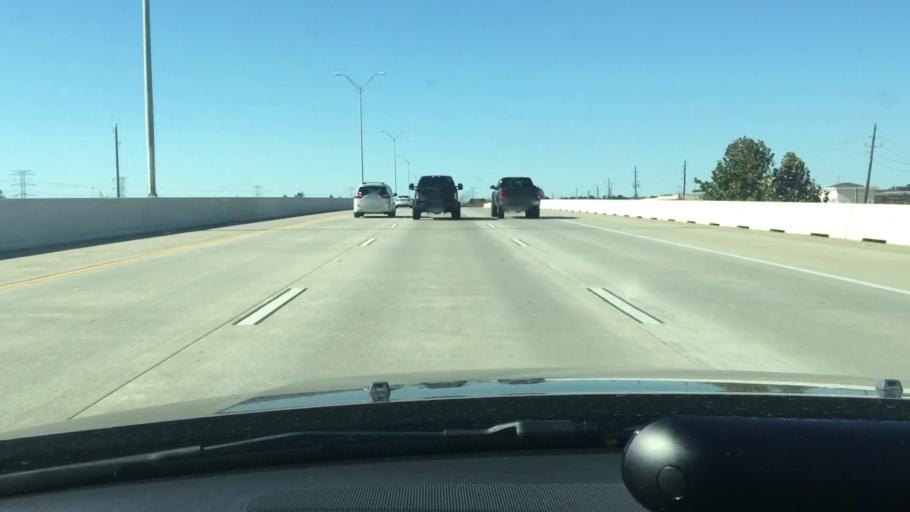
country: US
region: Texas
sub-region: Harris County
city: Humble
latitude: 29.9348
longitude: -95.2481
